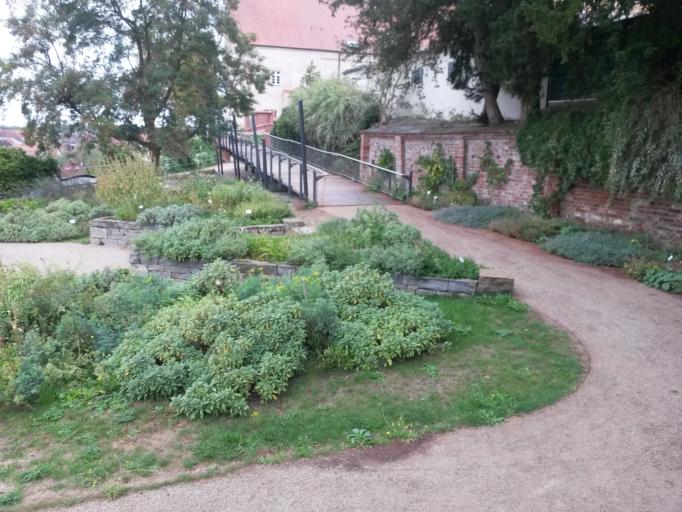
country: DE
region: Saxony-Anhalt
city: Havelberg
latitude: 52.8261
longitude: 12.0800
